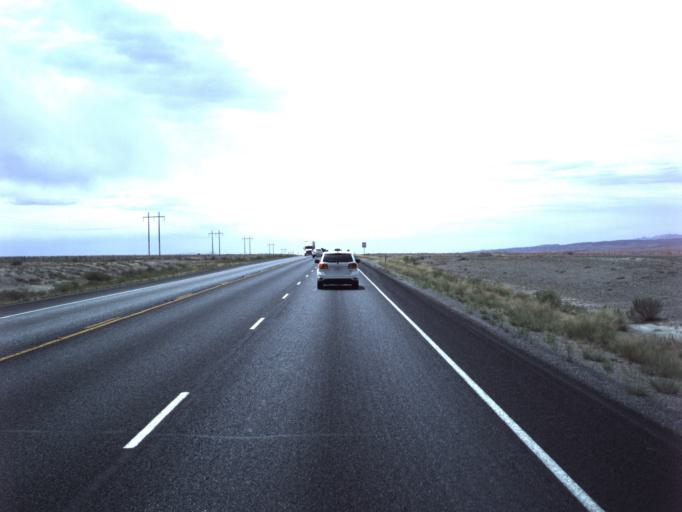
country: US
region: Utah
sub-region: Carbon County
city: East Carbon City
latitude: 39.1898
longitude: -110.3385
